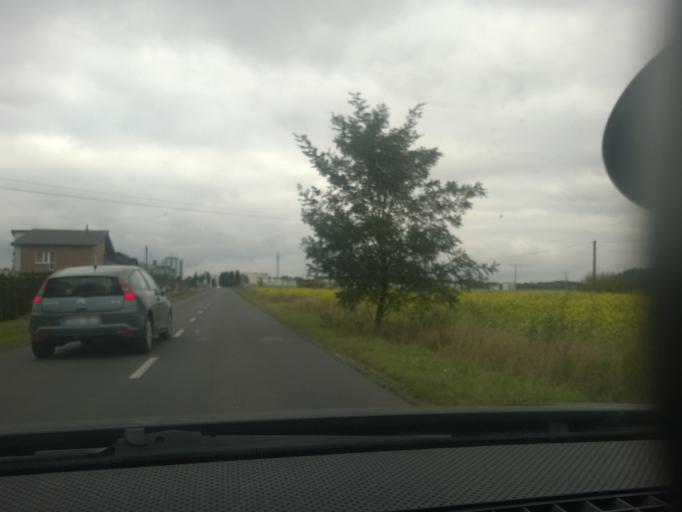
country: PL
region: Greater Poland Voivodeship
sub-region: Powiat kaliski
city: Opatowek
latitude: 51.7312
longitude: 18.1907
